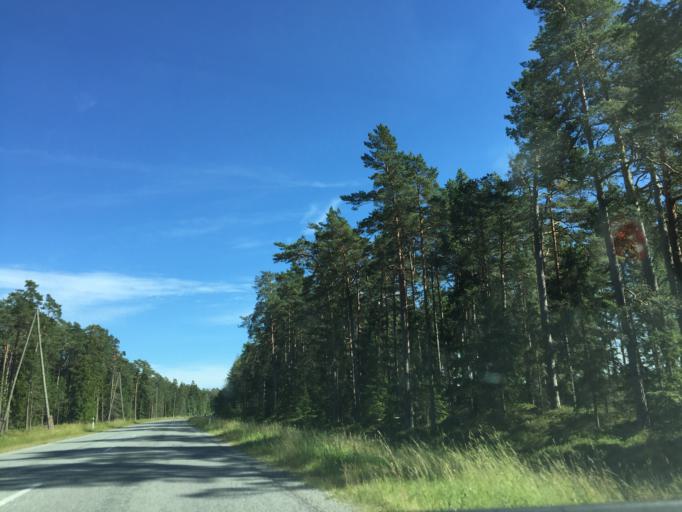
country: LV
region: Rojas
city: Roja
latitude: 57.4896
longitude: 22.8386
